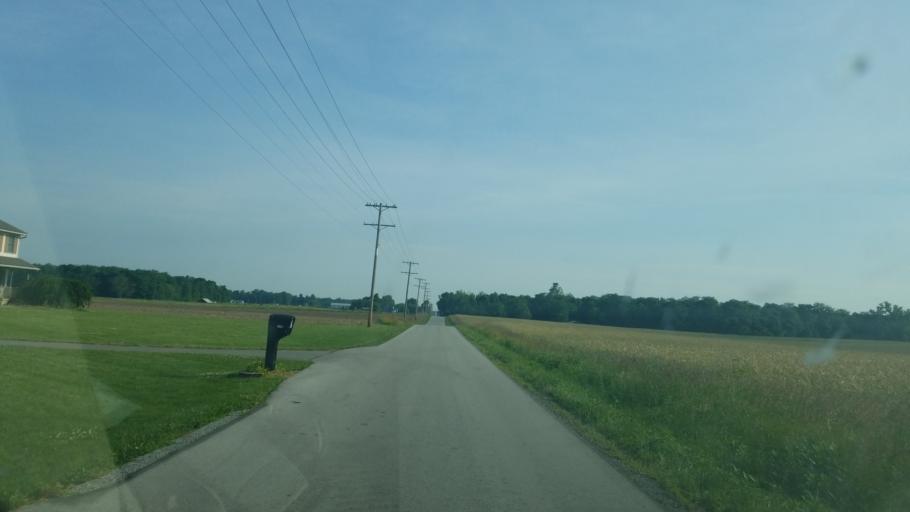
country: US
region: Ohio
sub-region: Hancock County
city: Arlington
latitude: 40.8584
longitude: -83.6702
